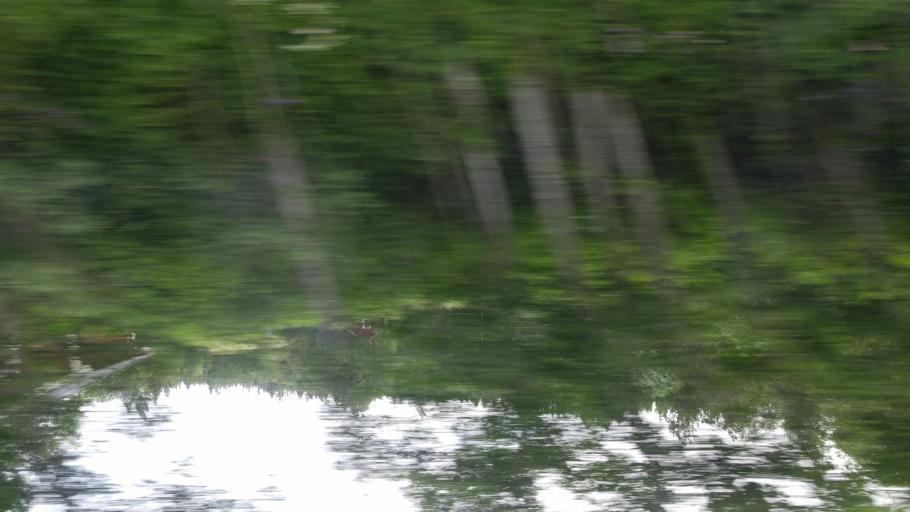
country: SE
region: Jaemtland
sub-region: Are Kommun
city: Are
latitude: 63.4005
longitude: 13.0049
